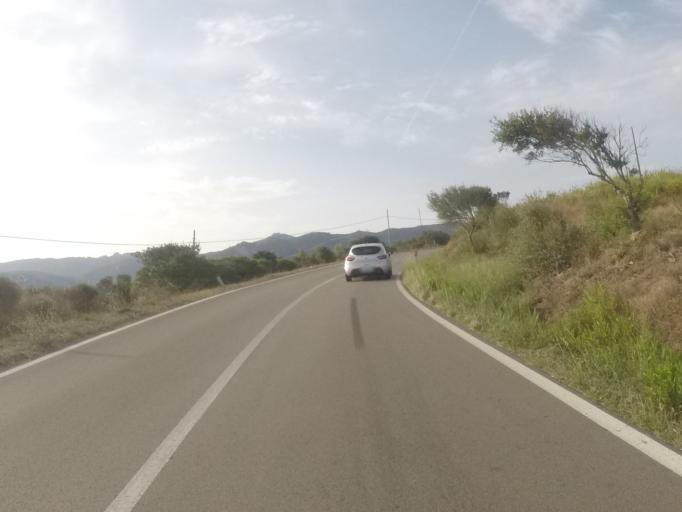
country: IT
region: Sardinia
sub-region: Provincia di Olbia-Tempio
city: Aglientu
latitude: 41.0893
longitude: 9.0271
